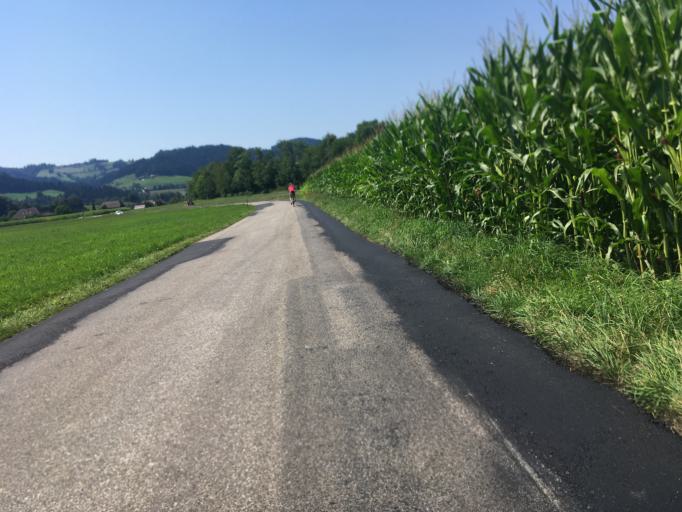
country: CH
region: Bern
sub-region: Emmental District
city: Langnau
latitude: 46.9435
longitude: 7.7703
